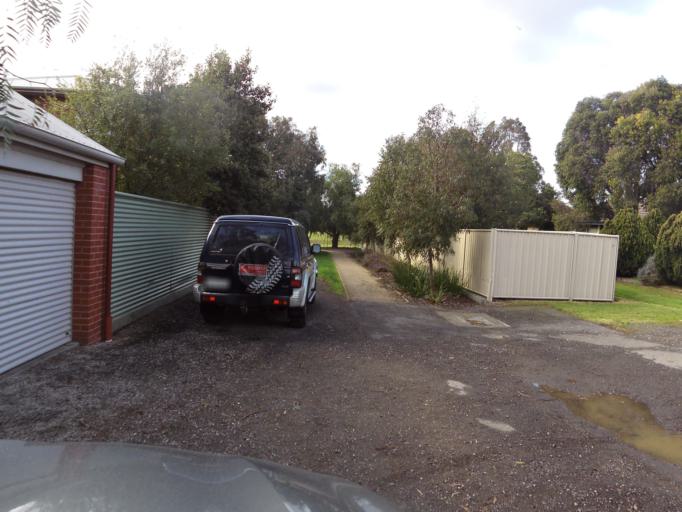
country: AU
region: Victoria
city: Spotswood
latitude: -37.8221
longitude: 144.8846
